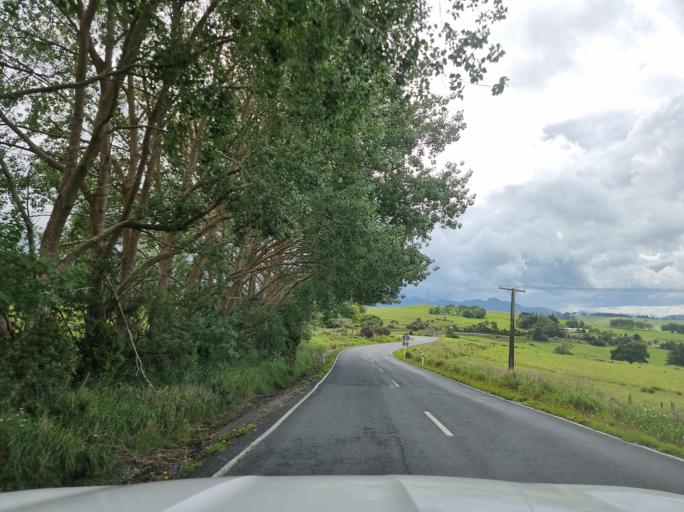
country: NZ
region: Northland
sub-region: Whangarei
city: Ruakaka
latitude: -35.9203
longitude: 174.2687
